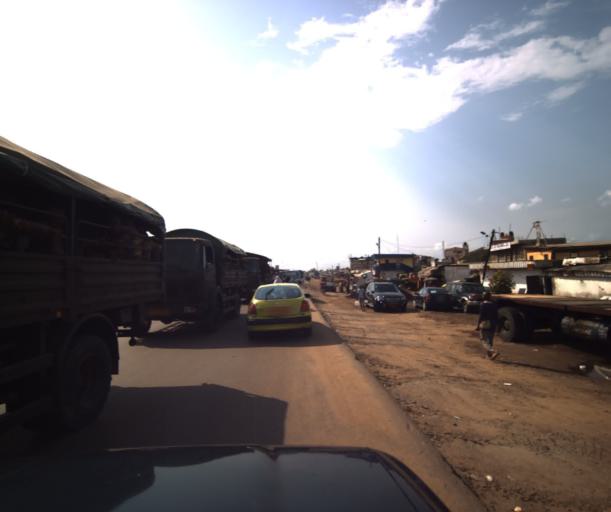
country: CM
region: Littoral
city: Douala
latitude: 4.0142
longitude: 9.7288
